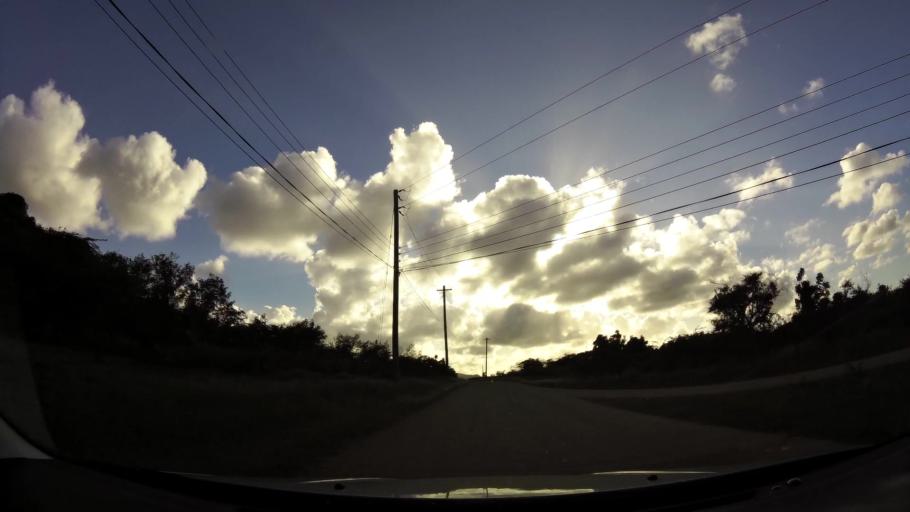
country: AG
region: Saint George
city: Piggotts
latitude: 17.1184
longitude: -61.7936
